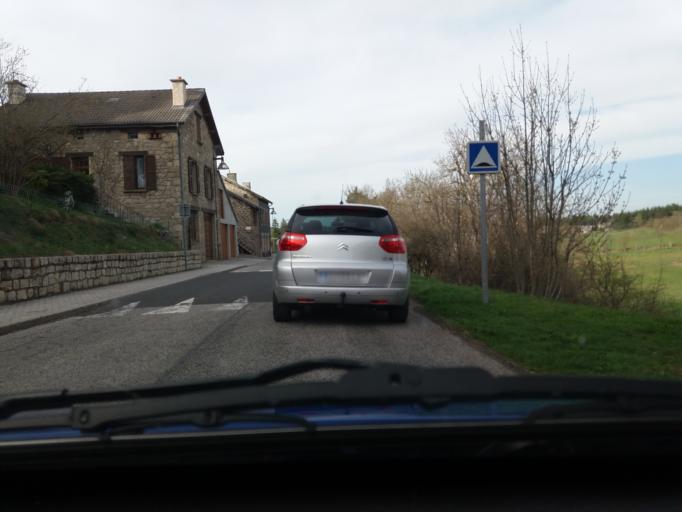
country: FR
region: Auvergne
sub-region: Departement de la Haute-Loire
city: Mazet-Saint-Voy
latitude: 45.0493
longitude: 4.2463
